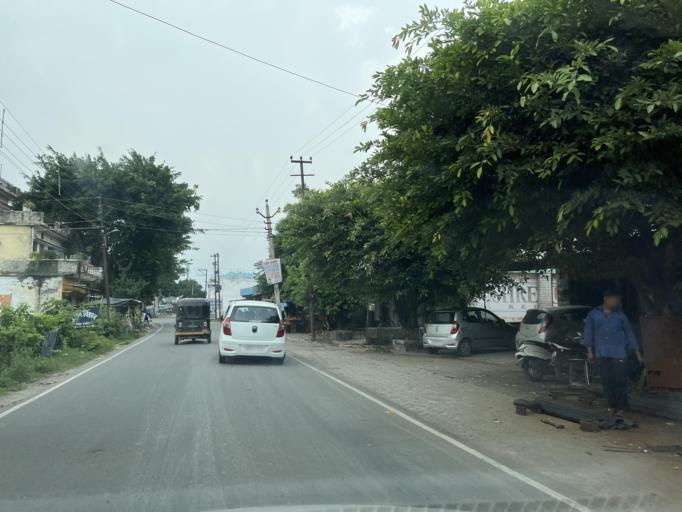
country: IN
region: Uttarakhand
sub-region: Naini Tal
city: Haldwani
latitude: 29.1995
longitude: 79.4867
